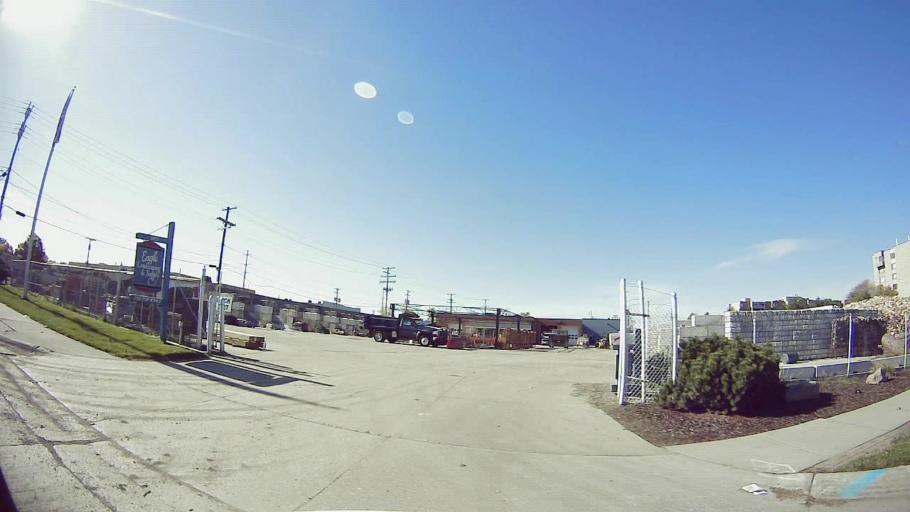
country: US
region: Michigan
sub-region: Oakland County
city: Southfield
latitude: 42.4449
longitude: -83.2591
